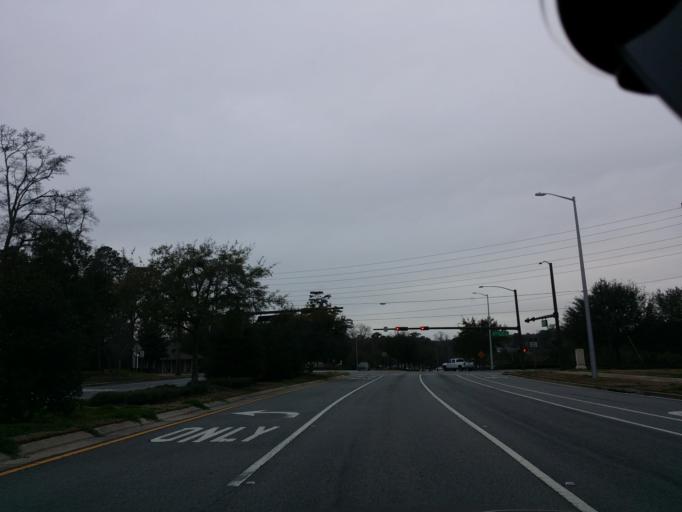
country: US
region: Florida
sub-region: Leon County
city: Tallahassee
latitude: 30.4785
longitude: -84.2331
